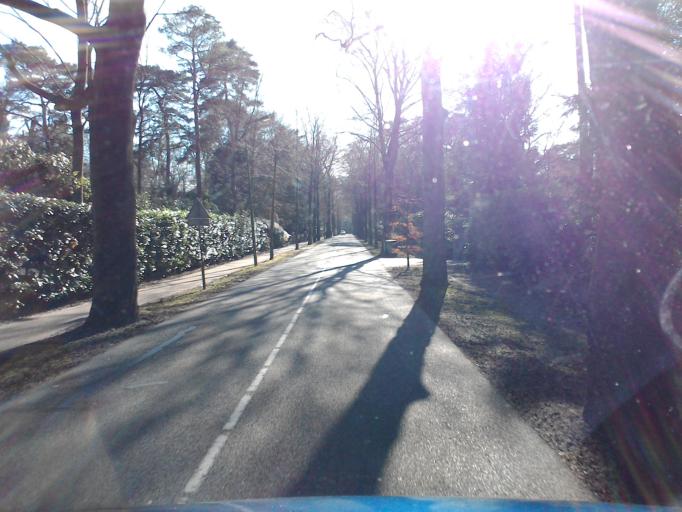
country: NL
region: Utrecht
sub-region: Gemeente De Bilt
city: De Bilt
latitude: 52.1443
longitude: 5.2171
